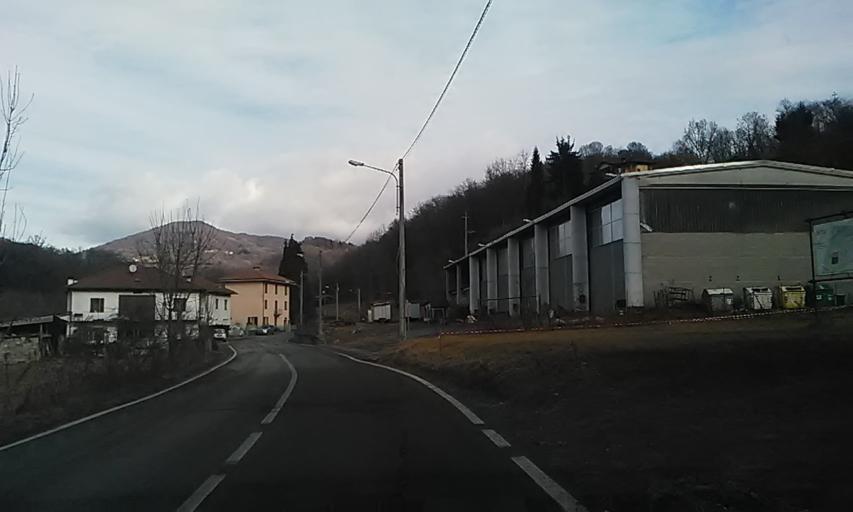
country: IT
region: Piedmont
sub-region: Provincia di Vercelli
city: Borgosesia
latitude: 45.7231
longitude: 8.2833
